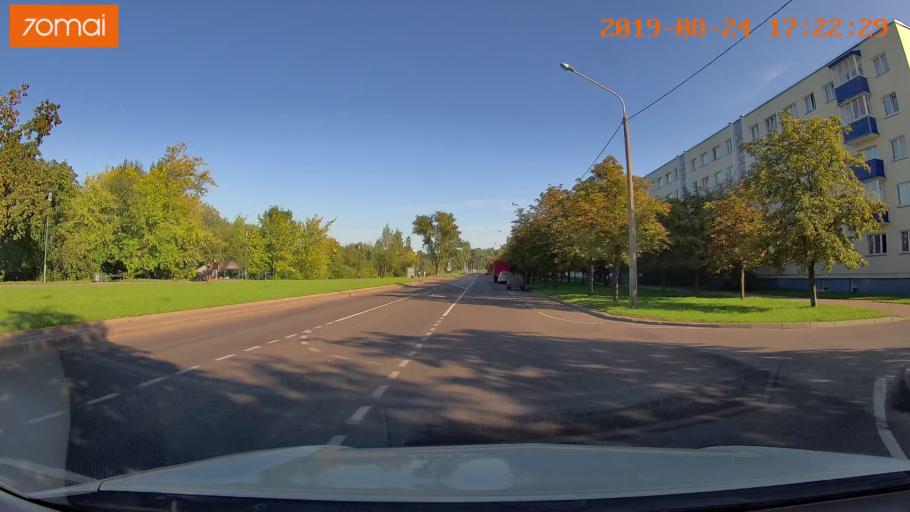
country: BY
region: Minsk
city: Hatava
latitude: 53.8456
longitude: 27.6448
